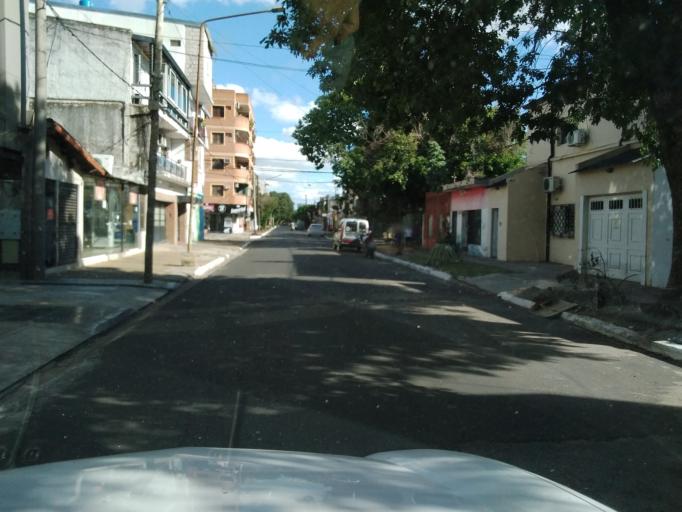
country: AR
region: Corrientes
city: Corrientes
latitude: -27.4785
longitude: -58.8316
